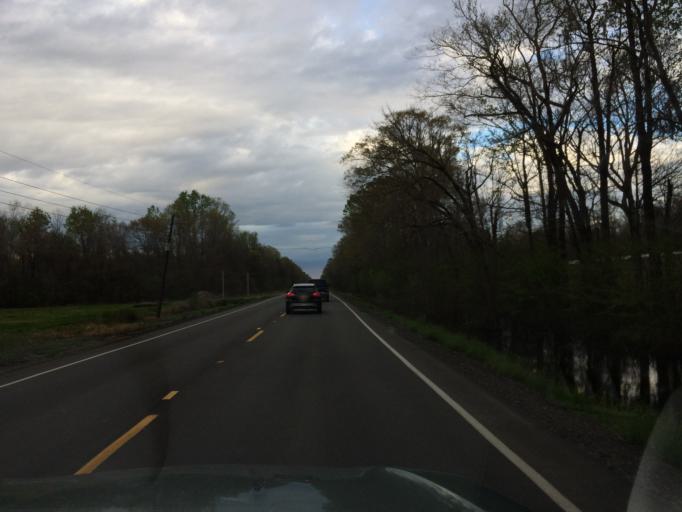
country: US
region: Louisiana
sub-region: West Baton Rouge Parish
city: Erwinville
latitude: 30.4620
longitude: -91.4174
